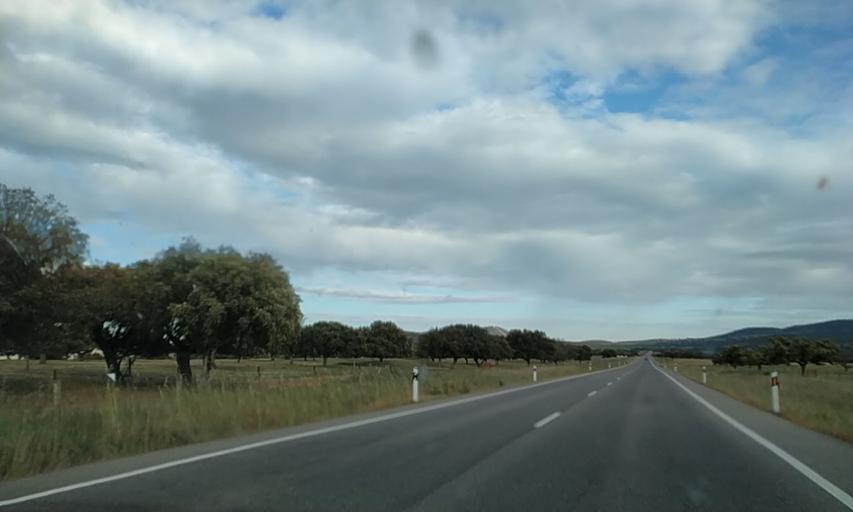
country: ES
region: Extremadura
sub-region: Provincia de Caceres
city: Torrejoncillo
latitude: 39.8702
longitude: -6.4405
